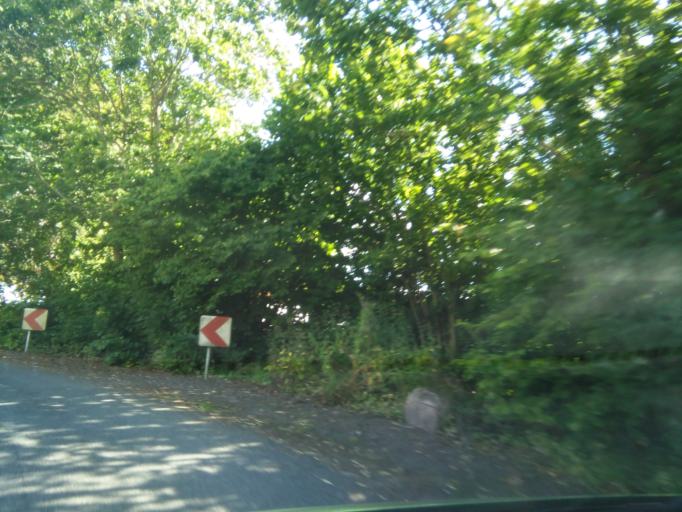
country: DK
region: Central Jutland
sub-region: Skanderborg Kommune
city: Horning
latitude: 56.1156
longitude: 10.0206
